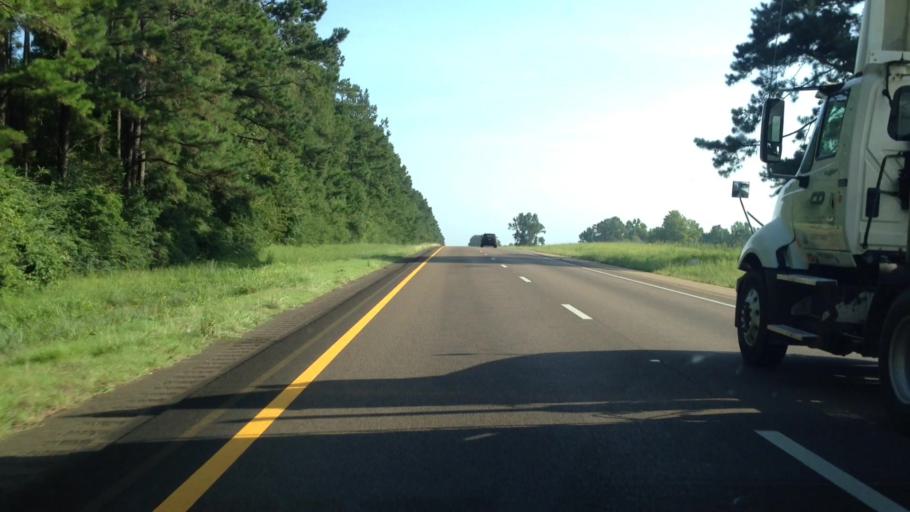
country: US
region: Mississippi
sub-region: Pike County
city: Summit
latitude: 31.3073
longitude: -90.4778
